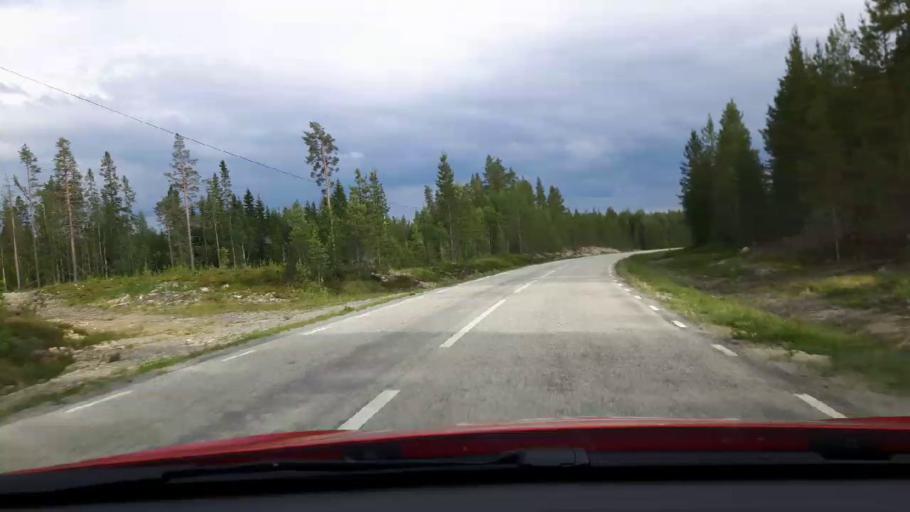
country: SE
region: Jaemtland
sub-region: Bergs Kommun
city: Hoverberg
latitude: 62.6604
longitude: 14.0549
